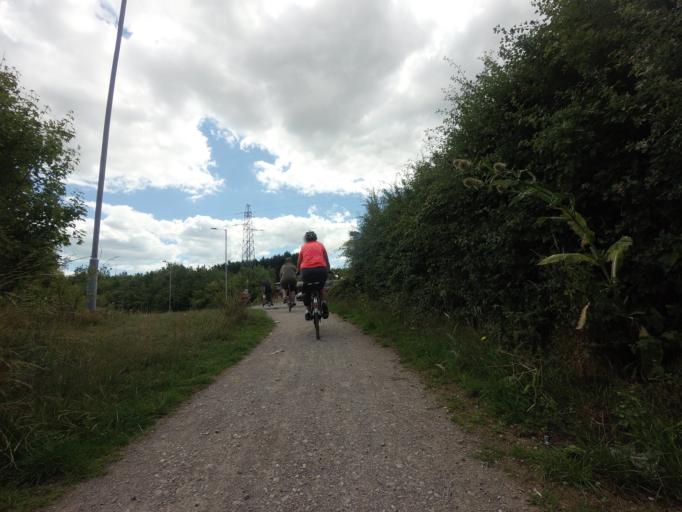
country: GB
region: England
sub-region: East Sussex
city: Hailsham
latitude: 50.8305
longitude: 0.2376
